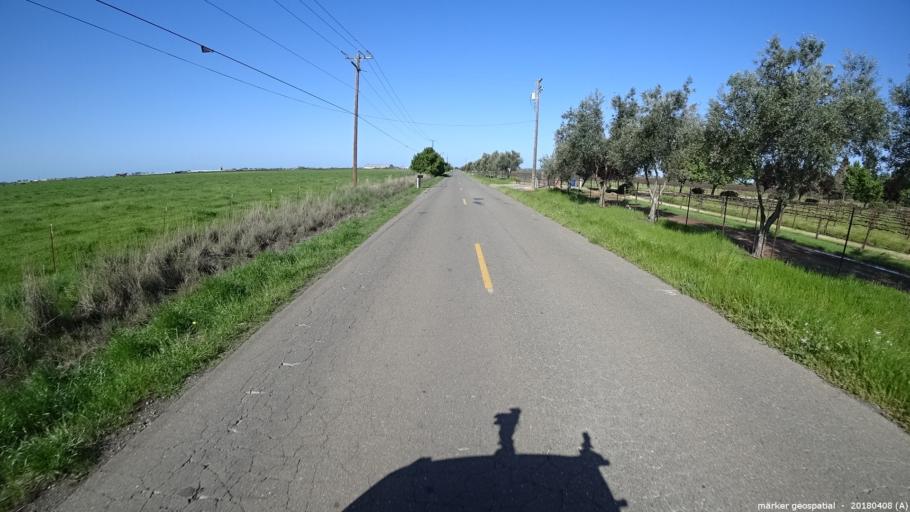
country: US
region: California
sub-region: Sacramento County
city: Elk Grove
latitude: 38.3508
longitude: -121.3811
